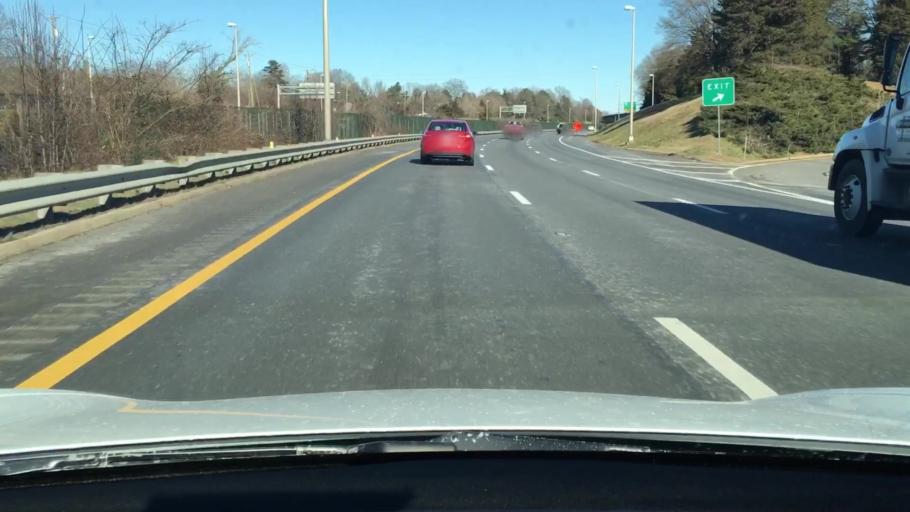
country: US
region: Virginia
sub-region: City of Richmond
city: Richmond
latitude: 37.5469
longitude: -77.4912
